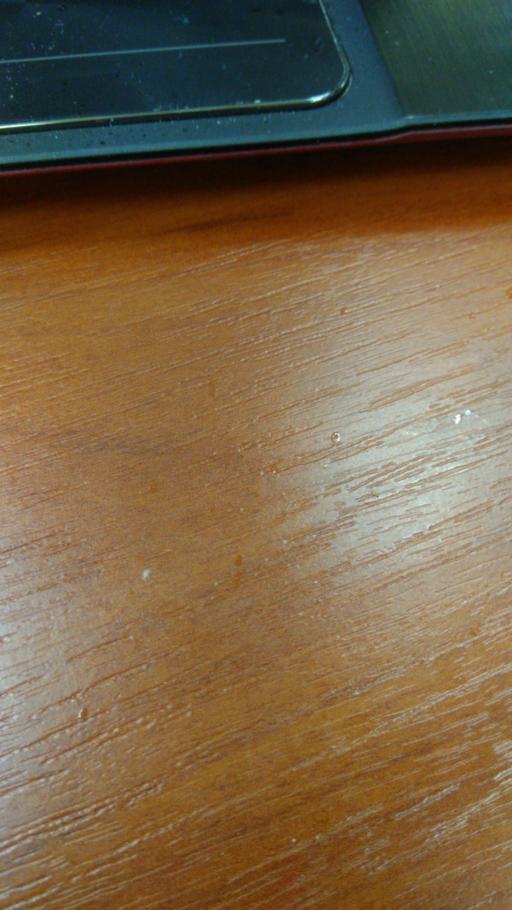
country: RU
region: Tverskaya
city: Emmaus
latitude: 56.7838
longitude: 36.0656
